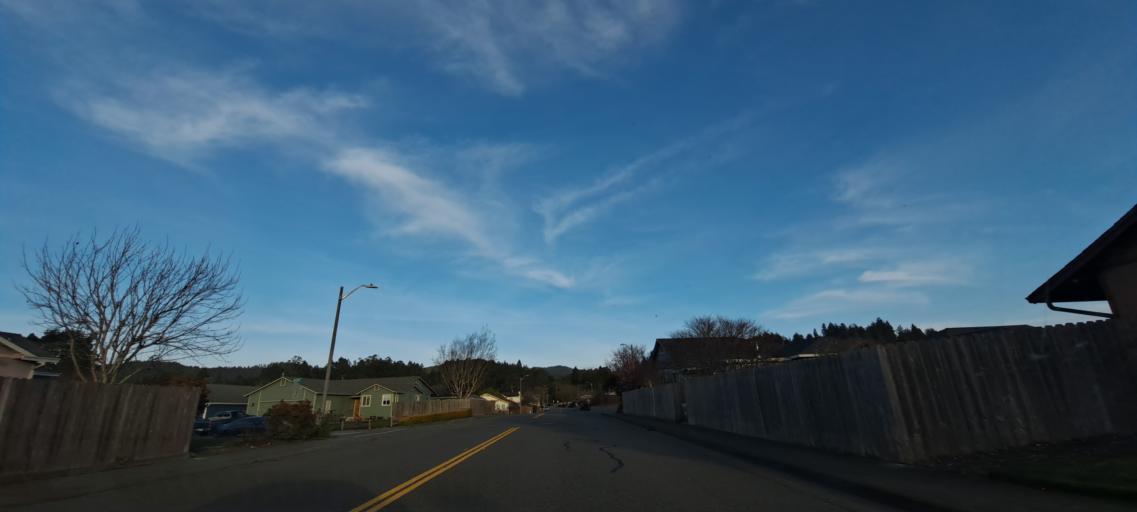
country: US
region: California
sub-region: Humboldt County
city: Fortuna
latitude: 40.5778
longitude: -124.1332
